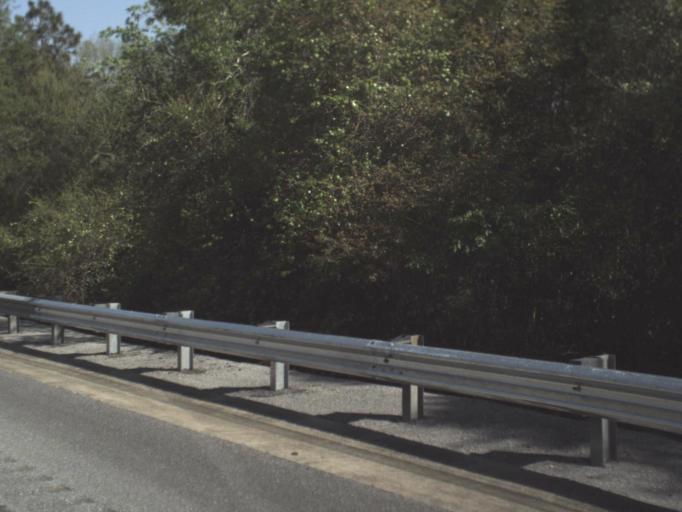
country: US
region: Florida
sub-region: Okaloosa County
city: Crestview
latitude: 30.7165
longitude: -86.6534
